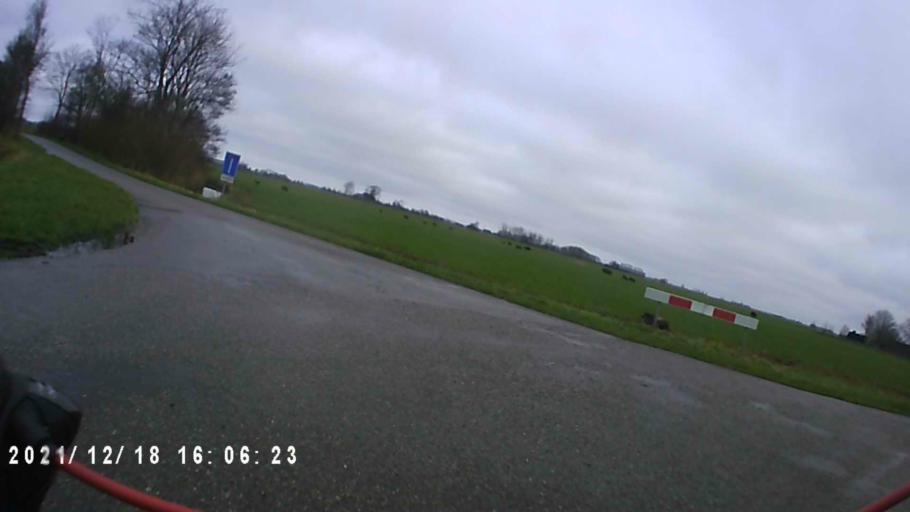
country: NL
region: Friesland
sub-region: Gemeente Dongeradeel
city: Anjum
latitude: 53.3564
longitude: 6.0772
